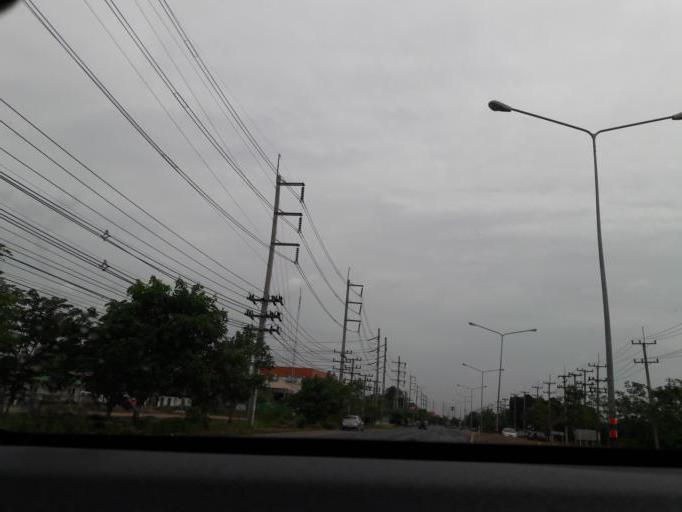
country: TH
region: Ratchaburi
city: Damnoen Saduak
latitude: 13.5815
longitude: 99.9670
